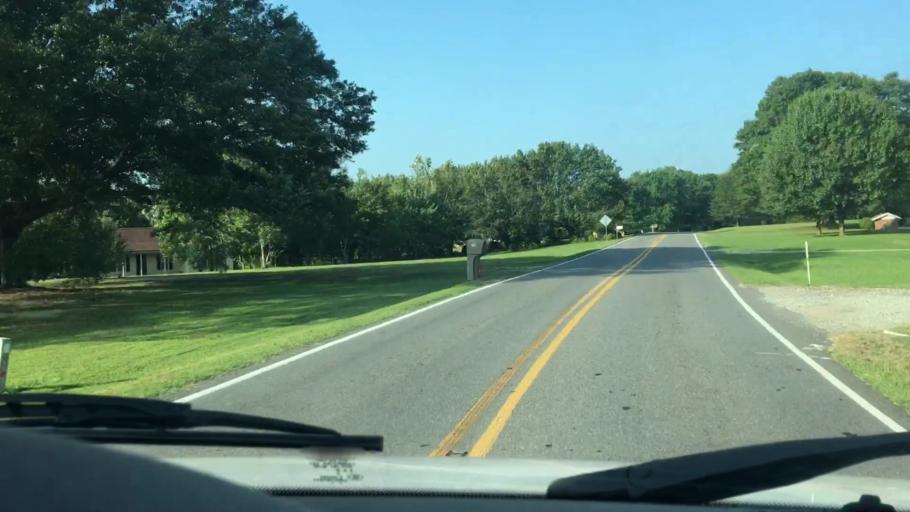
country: US
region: North Carolina
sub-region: Lincoln County
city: Lowesville
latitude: 35.4426
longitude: -80.9908
